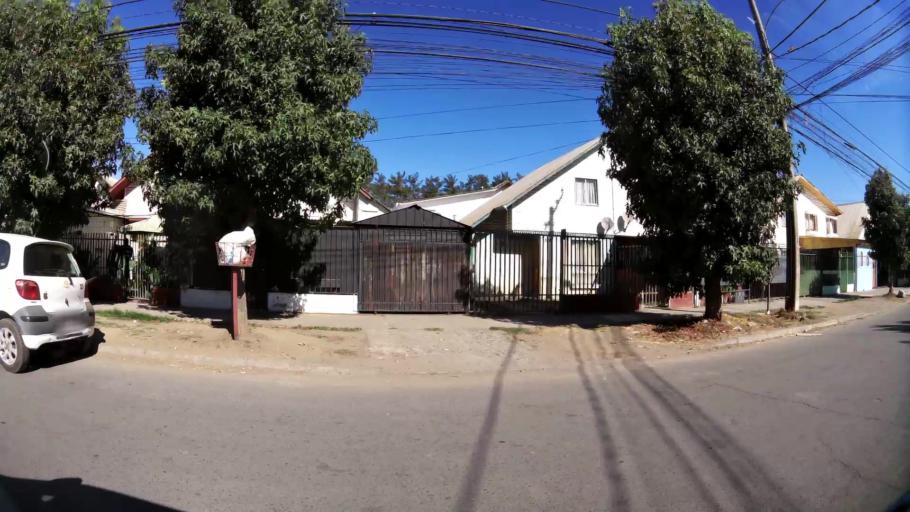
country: CL
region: O'Higgins
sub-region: Provincia de Colchagua
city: Chimbarongo
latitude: -34.5782
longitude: -70.9999
